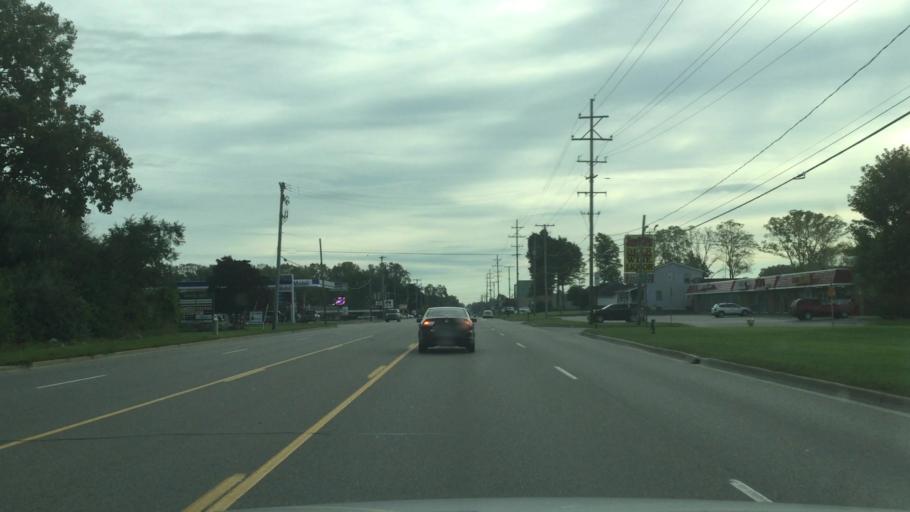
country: US
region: Michigan
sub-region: Genesee County
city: Flint
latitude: 42.9738
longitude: -83.7087
